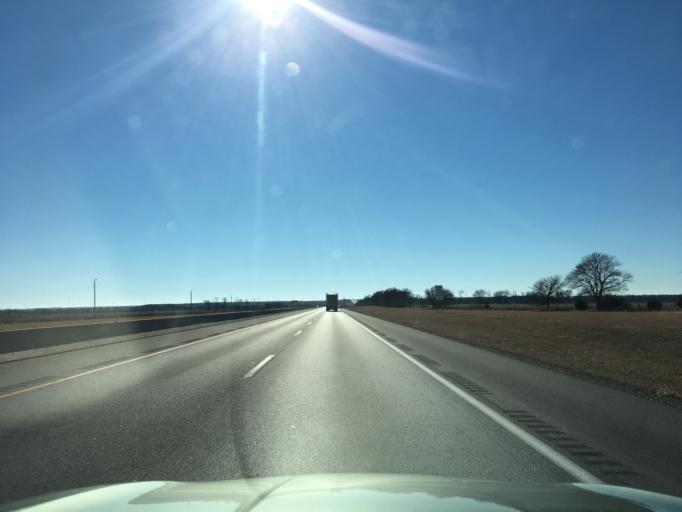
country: US
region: Kansas
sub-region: Sumner County
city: Wellington
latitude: 37.2299
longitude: -97.3388
